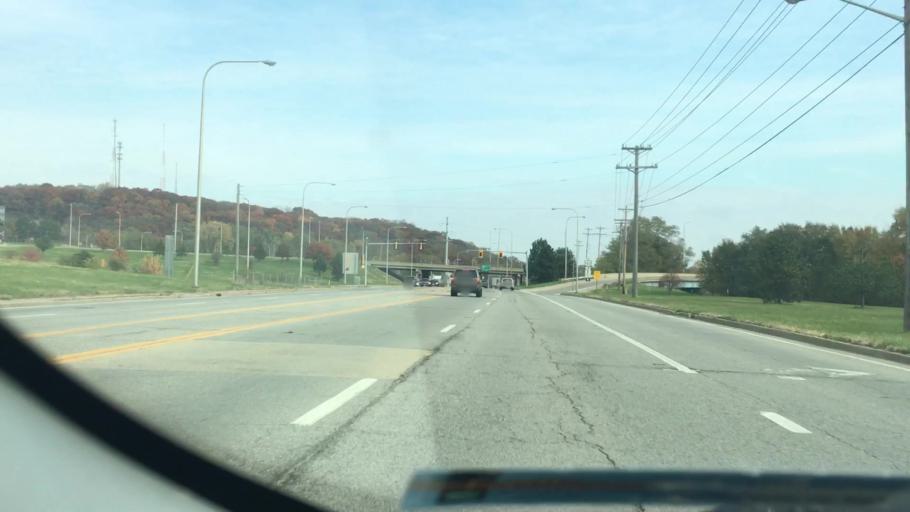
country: US
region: Illinois
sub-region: Peoria County
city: North Peoria
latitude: 40.7206
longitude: -89.5569
